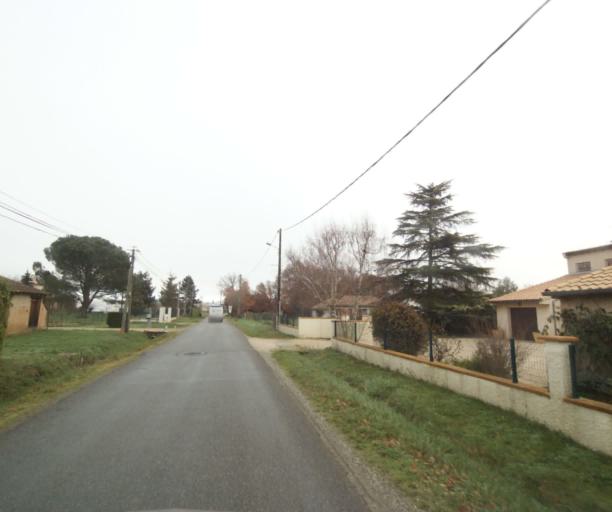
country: FR
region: Midi-Pyrenees
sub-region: Departement de la Haute-Garonne
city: Villemur-sur-Tarn
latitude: 43.8571
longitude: 1.4727
